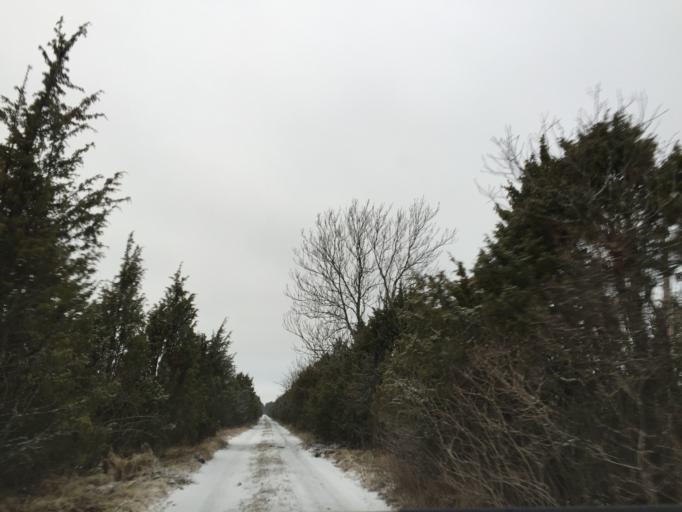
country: EE
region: Saare
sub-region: Orissaare vald
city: Orissaare
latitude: 58.5470
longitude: 23.3900
